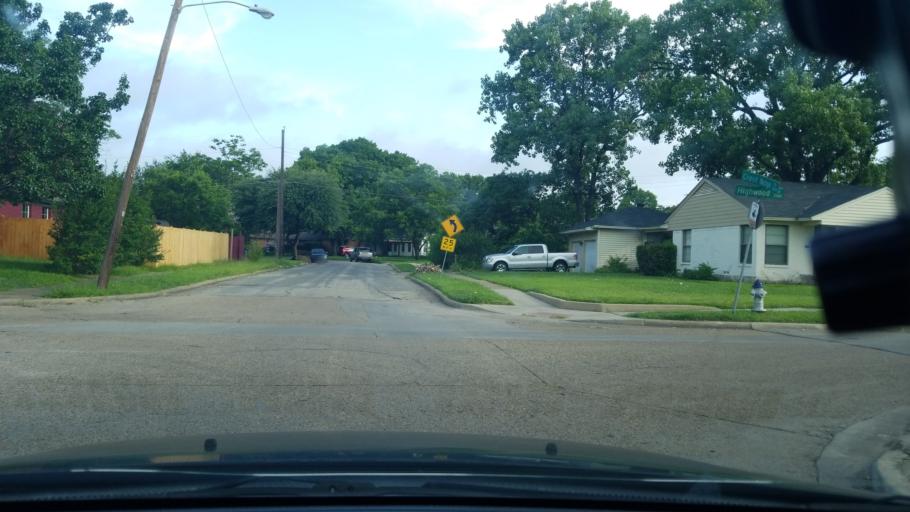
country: US
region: Texas
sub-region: Dallas County
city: Garland
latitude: 32.8296
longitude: -96.6657
